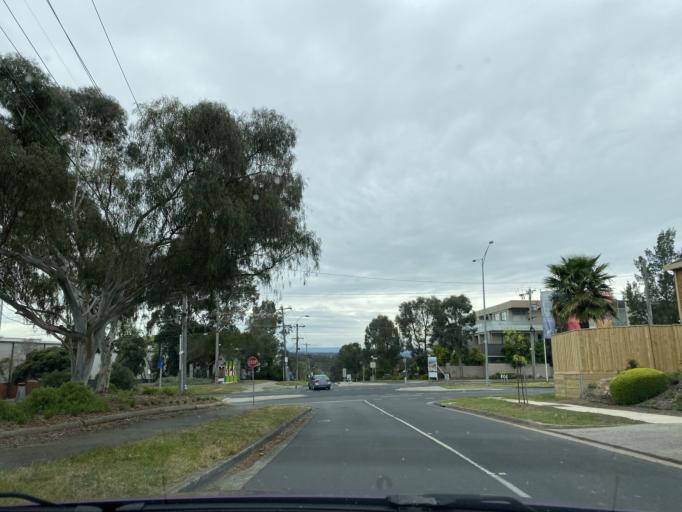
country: AU
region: Victoria
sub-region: Manningham
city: Templestowe Lower
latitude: -37.7596
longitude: 145.1298
